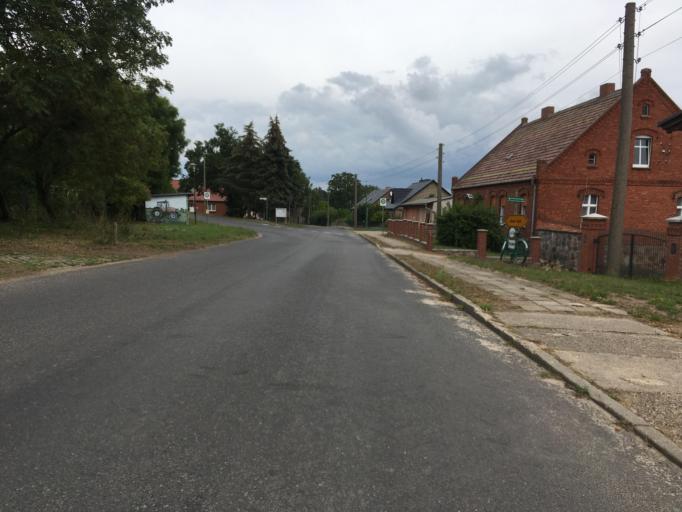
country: DE
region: Brandenburg
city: Prenzlau
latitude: 53.2601
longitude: 13.8475
